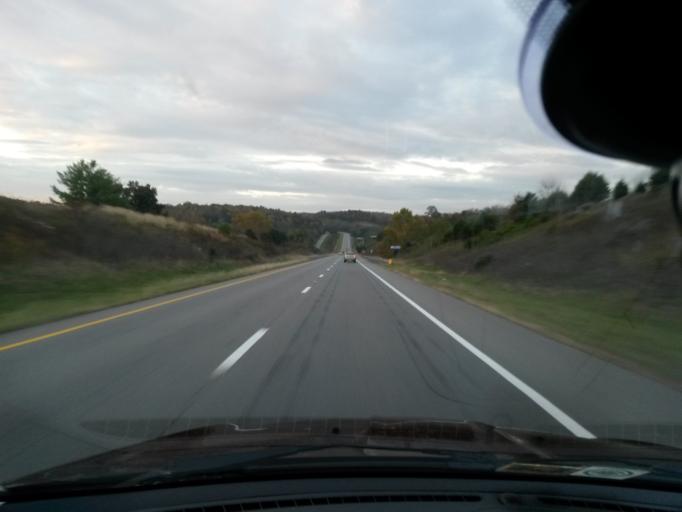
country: US
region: Virginia
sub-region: Botetourt County
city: Fincastle
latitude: 37.6113
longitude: -79.8321
